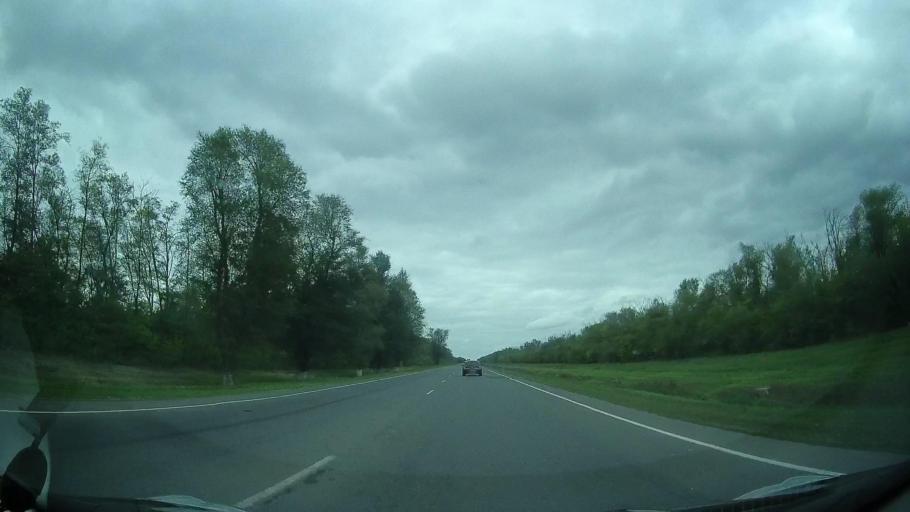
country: RU
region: Rostov
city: Yegorlykskaya
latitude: 46.5940
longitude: 40.6252
